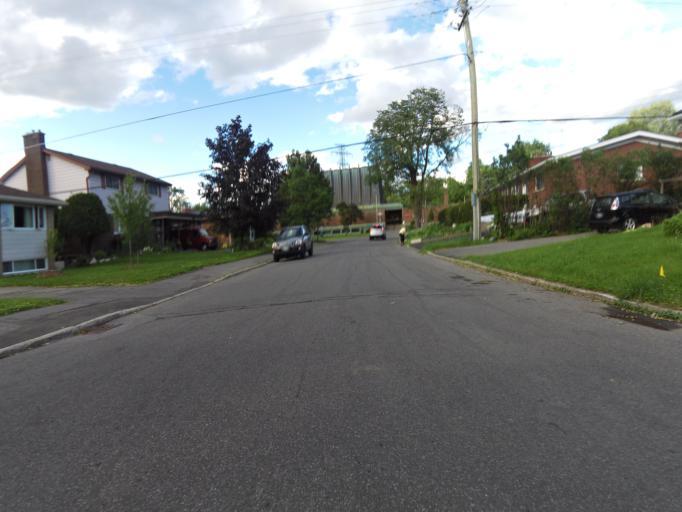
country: CA
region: Ontario
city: Ottawa
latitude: 45.3662
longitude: -75.7518
